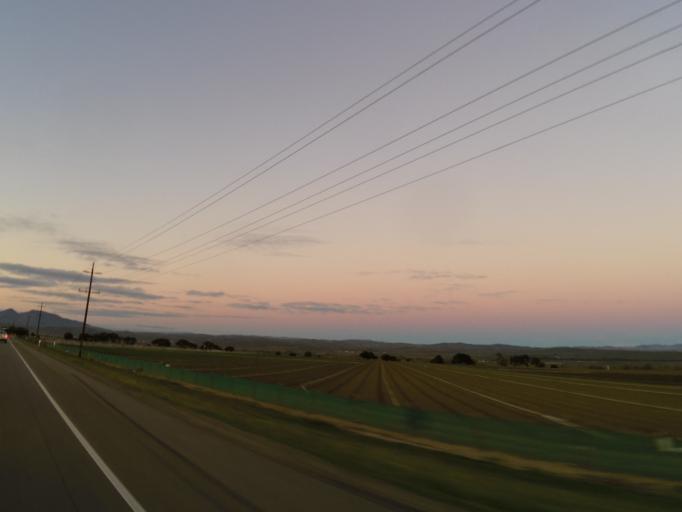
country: US
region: California
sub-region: Monterey County
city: King City
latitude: 36.2481
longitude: -121.1758
